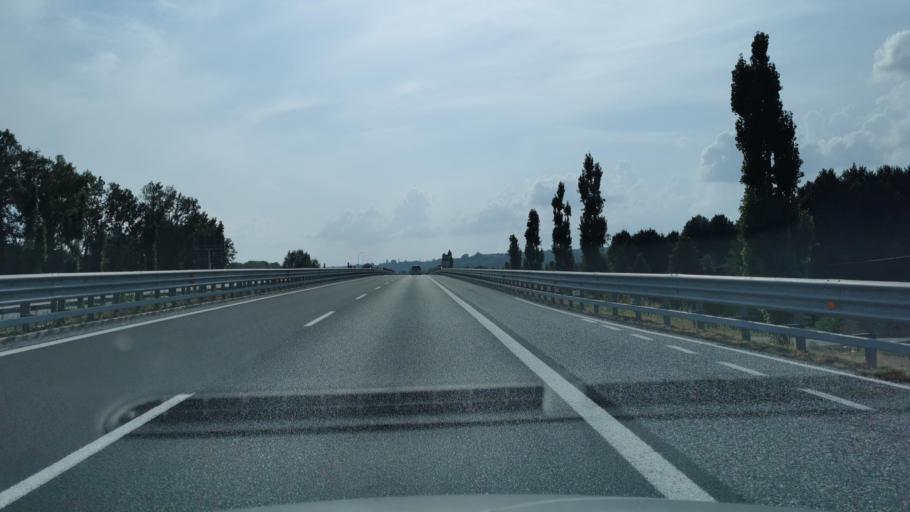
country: IT
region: Piedmont
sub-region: Provincia di Cuneo
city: Cherasco
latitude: 44.6627
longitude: 7.8568
